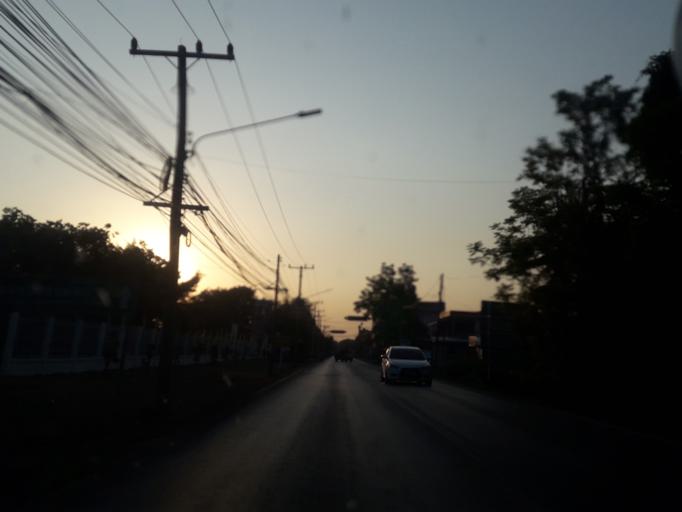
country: TH
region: Pathum Thani
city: Nong Suea
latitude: 14.1323
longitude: 100.8229
